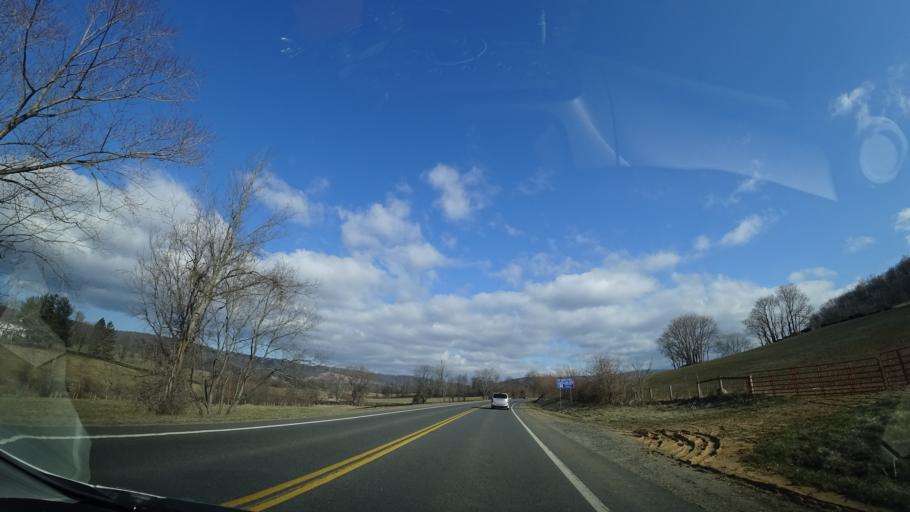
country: US
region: Virginia
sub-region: Warren County
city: Shenandoah Farms
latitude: 38.9727
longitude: -77.9529
